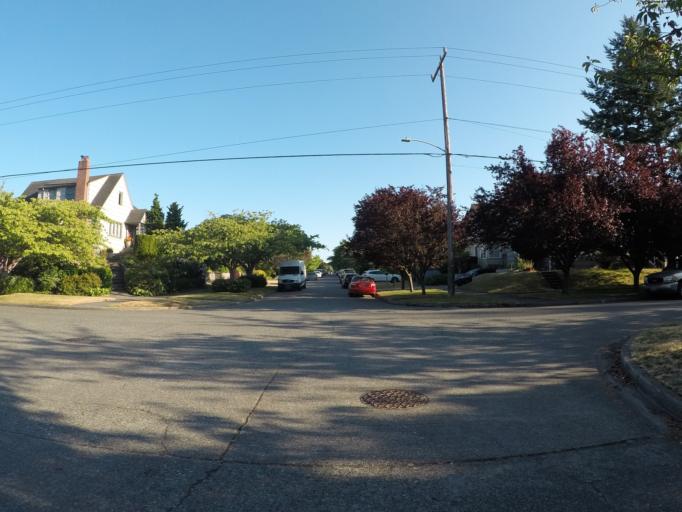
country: US
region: Washington
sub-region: King County
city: Seattle
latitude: 47.5882
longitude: -122.3876
